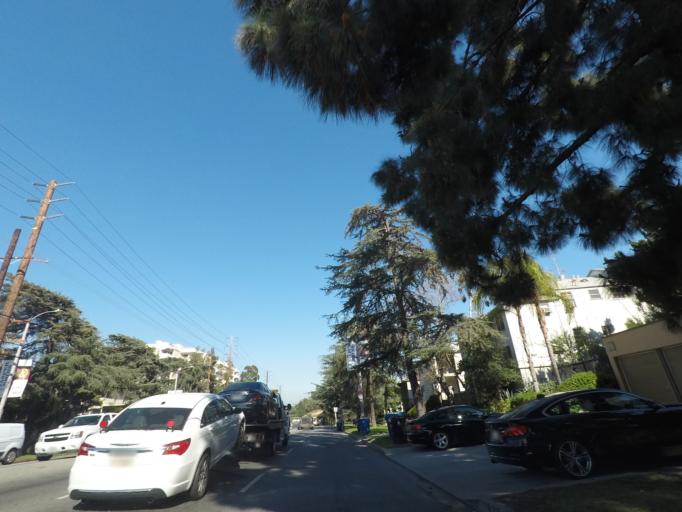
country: US
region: California
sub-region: Los Angeles County
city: Silver Lake
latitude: 34.1131
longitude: -118.2801
